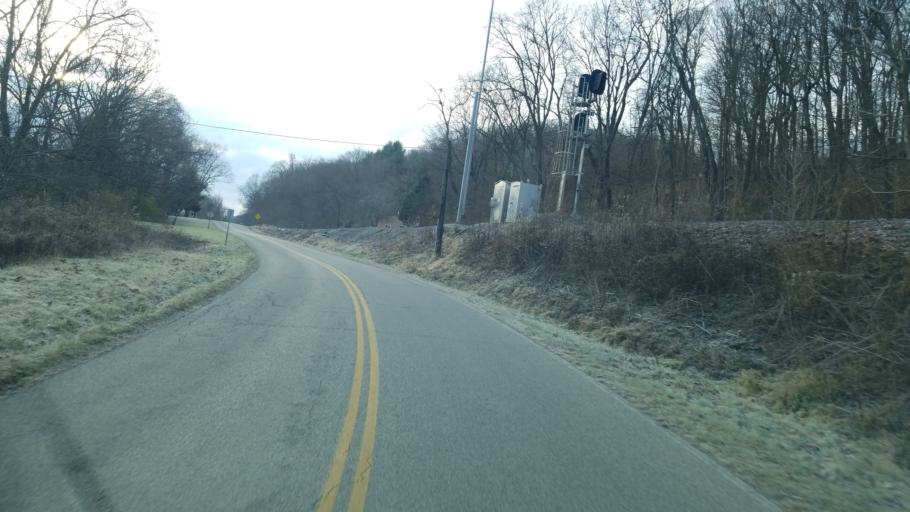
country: US
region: Ohio
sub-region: Ross County
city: Chillicothe
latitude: 39.2575
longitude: -82.9135
